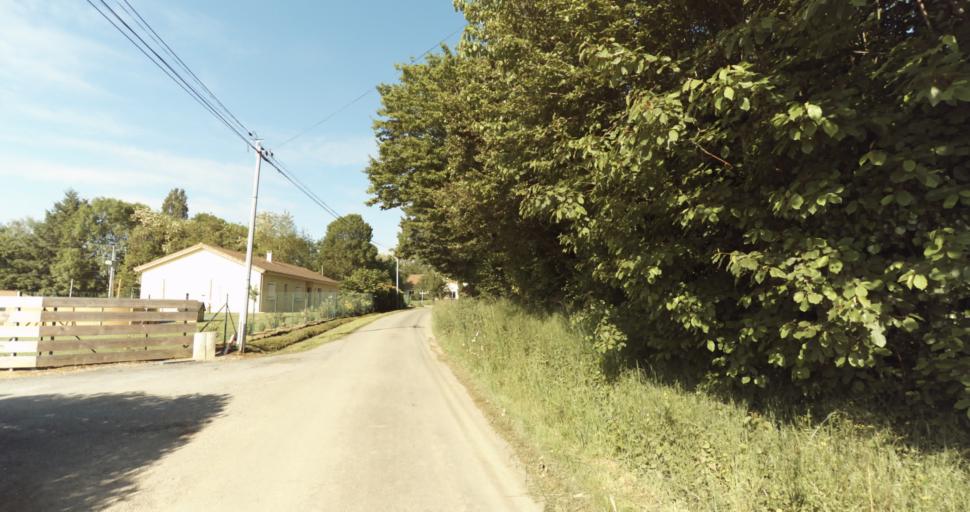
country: FR
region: Limousin
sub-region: Departement de la Haute-Vienne
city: Solignac
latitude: 45.7445
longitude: 1.2753
